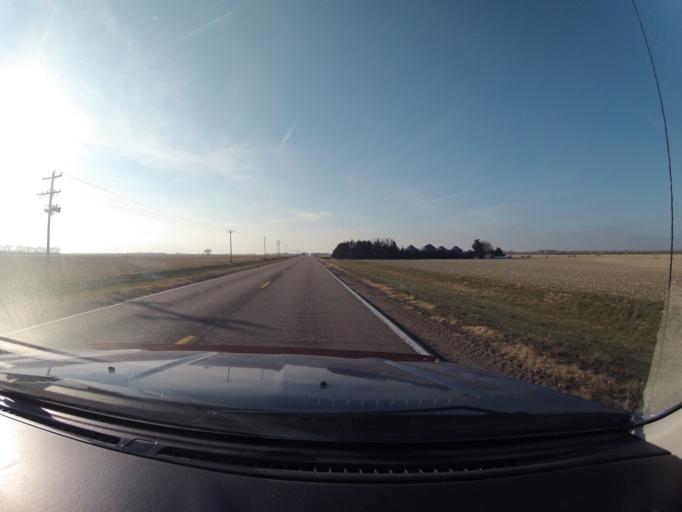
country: US
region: Nebraska
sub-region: Buffalo County
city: Kearney
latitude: 40.6410
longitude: -99.0535
